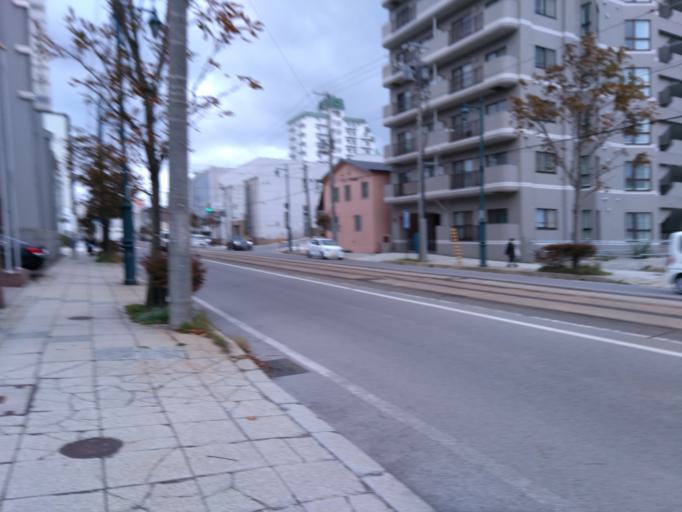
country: JP
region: Hokkaido
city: Hakodate
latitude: 41.7662
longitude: 140.7133
